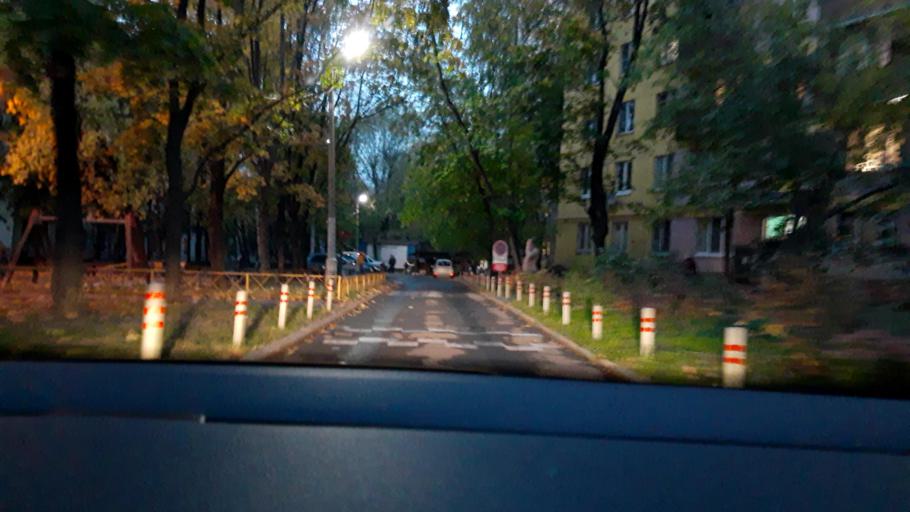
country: RU
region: Moscow
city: Novokuz'minki
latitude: 55.7127
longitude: 37.7766
